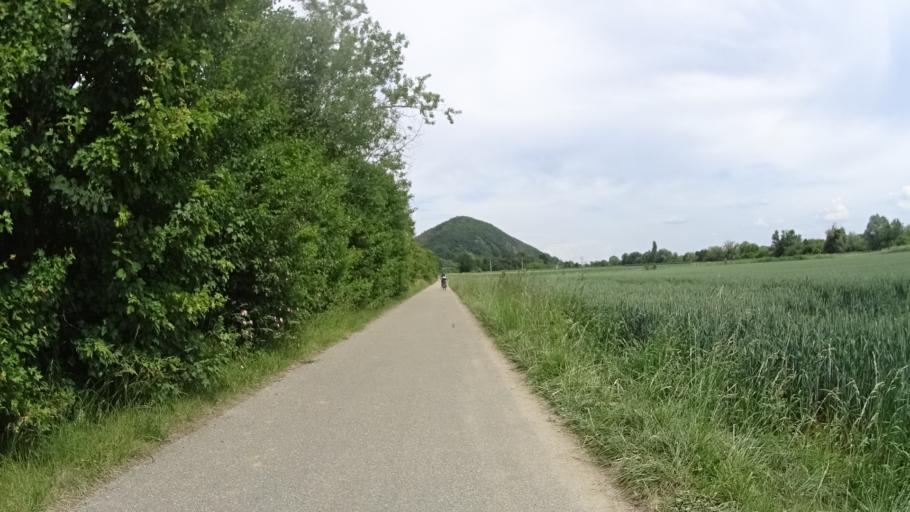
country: DE
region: Bavaria
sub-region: Upper Palatinate
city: Donaustauf
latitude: 49.0289
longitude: 12.2271
